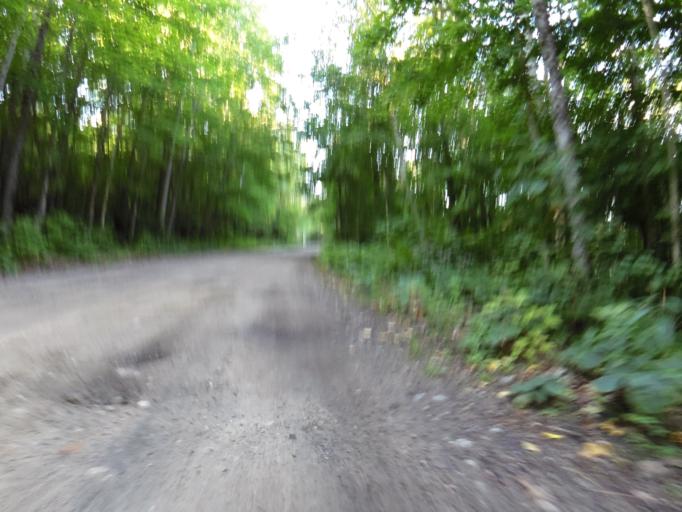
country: CA
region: Quebec
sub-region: Outaouais
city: Maniwaki
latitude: 46.3159
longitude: -76.0078
